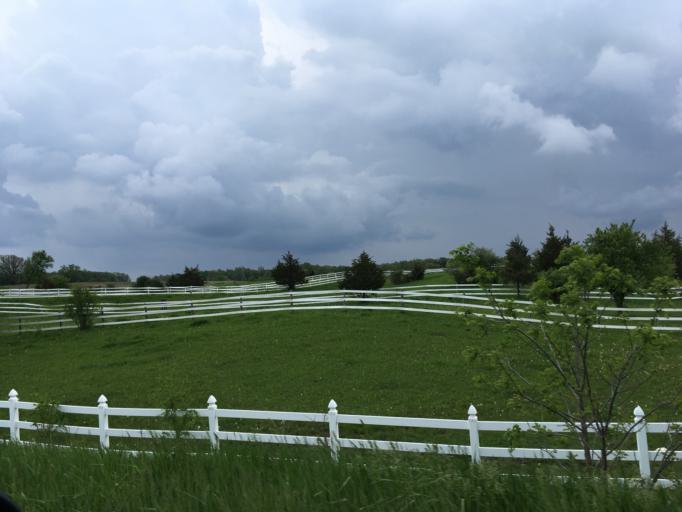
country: US
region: Michigan
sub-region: Lenawee County
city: Clinton
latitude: 42.1604
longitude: -83.9109
